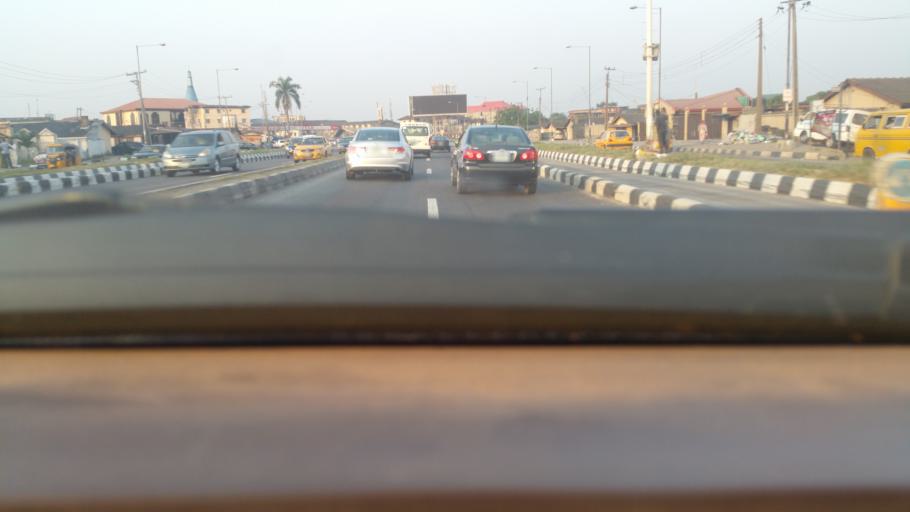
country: NG
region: Lagos
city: Surulere
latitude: 6.5028
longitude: 3.3635
